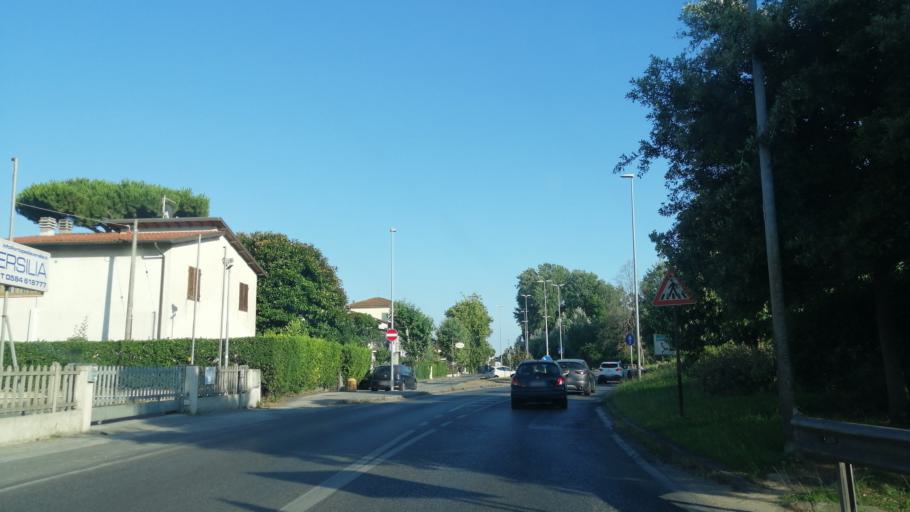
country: IT
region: Tuscany
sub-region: Provincia di Lucca
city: Camaiore
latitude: 43.9114
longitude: 10.2238
